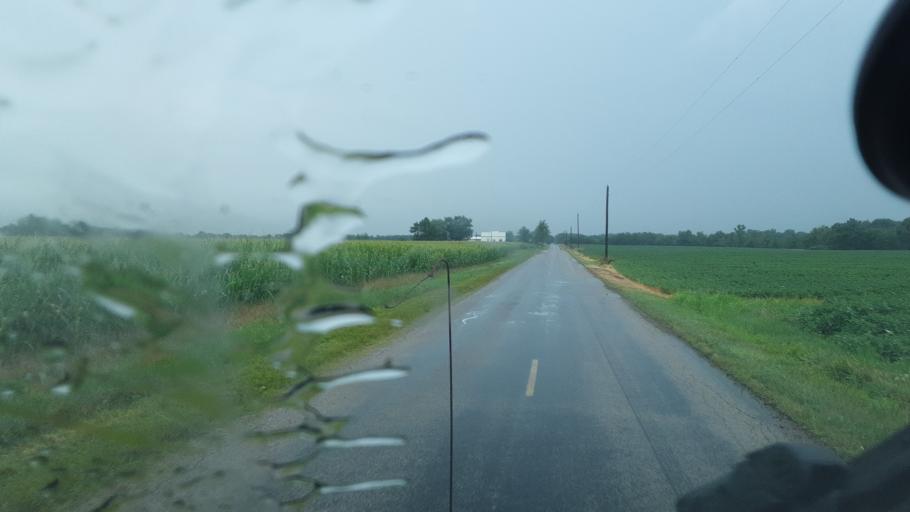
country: US
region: Ohio
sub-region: Williams County
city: Edgerton
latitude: 41.4994
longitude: -84.8149
